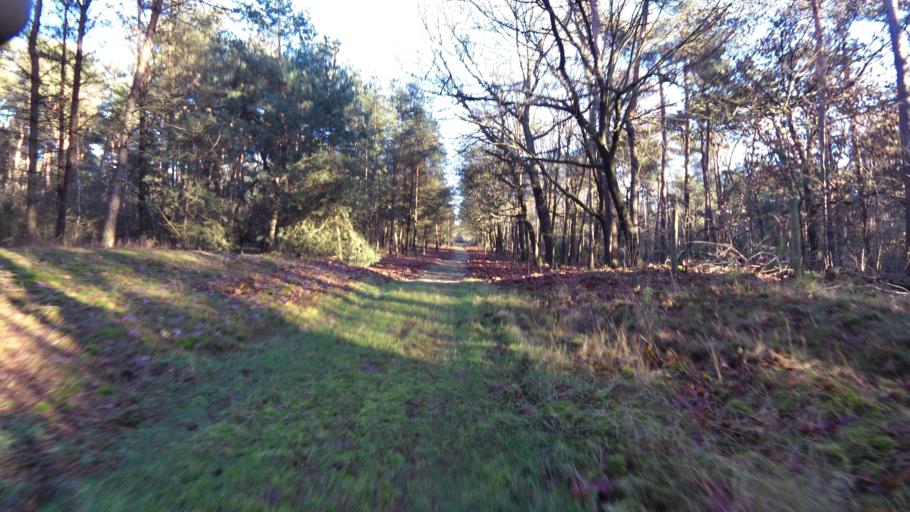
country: NL
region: Gelderland
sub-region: Gemeente Barneveld
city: Garderen
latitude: 52.2103
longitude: 5.7195
